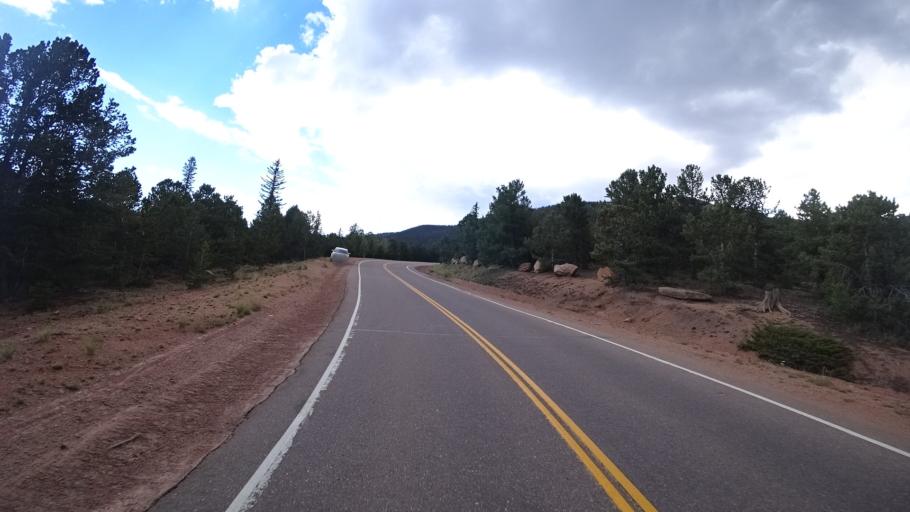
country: US
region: Colorado
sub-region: El Paso County
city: Cascade-Chipita Park
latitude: 38.8986
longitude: -105.0659
